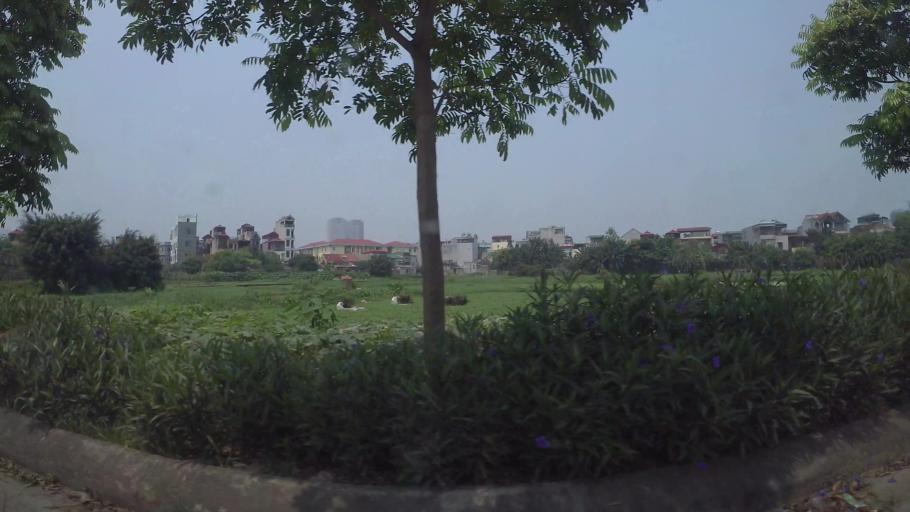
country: VN
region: Ha Noi
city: Van Dien
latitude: 20.9500
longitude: 105.8374
